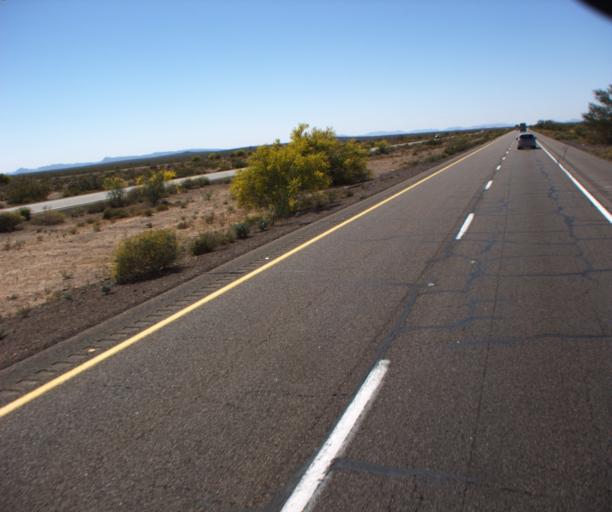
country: US
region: Arizona
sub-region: Maricopa County
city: Gila Bend
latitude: 32.8662
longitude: -113.1560
